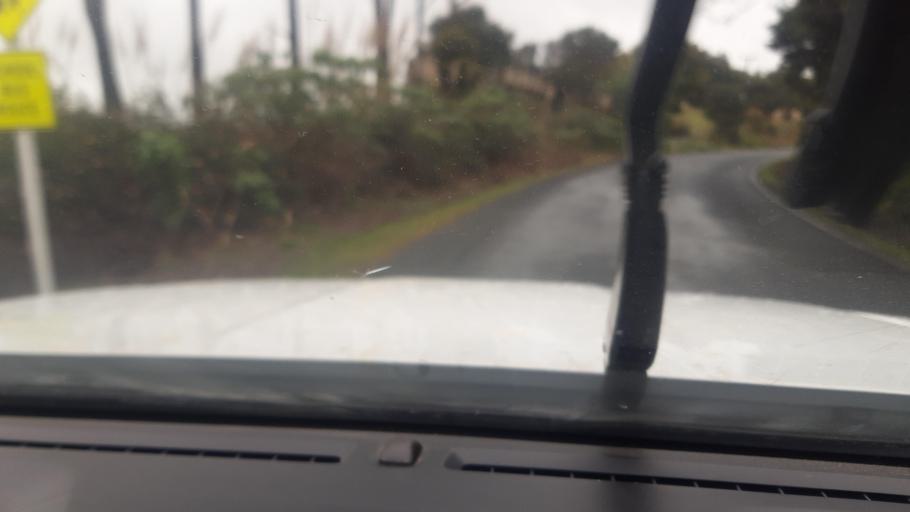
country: NZ
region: Northland
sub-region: Far North District
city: Kaitaia
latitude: -34.9954
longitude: 173.2175
